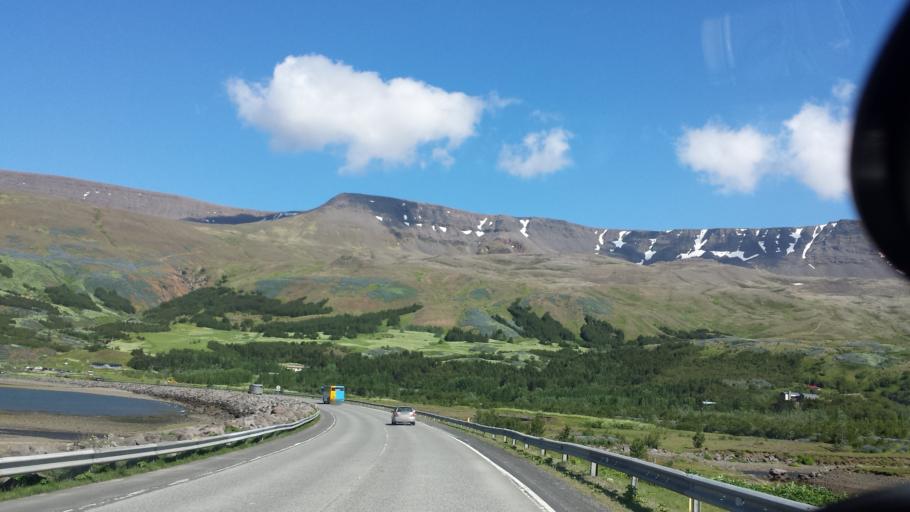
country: IS
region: Capital Region
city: Mosfellsbaer
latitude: 64.2034
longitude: -21.7079
